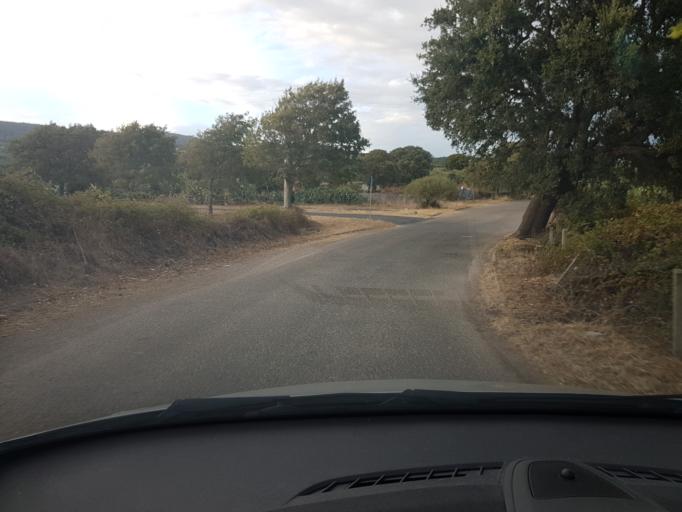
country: IT
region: Sardinia
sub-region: Provincia di Oristano
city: Seneghe
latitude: 40.0857
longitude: 8.6181
